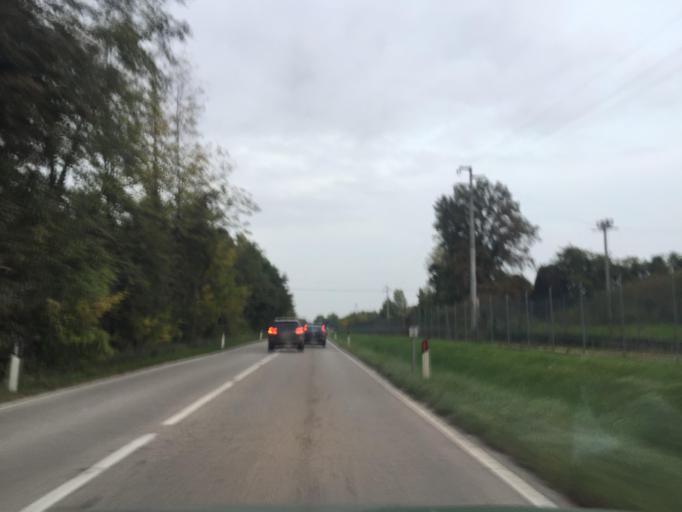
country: IT
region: Friuli Venezia Giulia
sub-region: Provincia di Pordenone
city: Fanna
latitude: 46.1731
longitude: 12.7351
